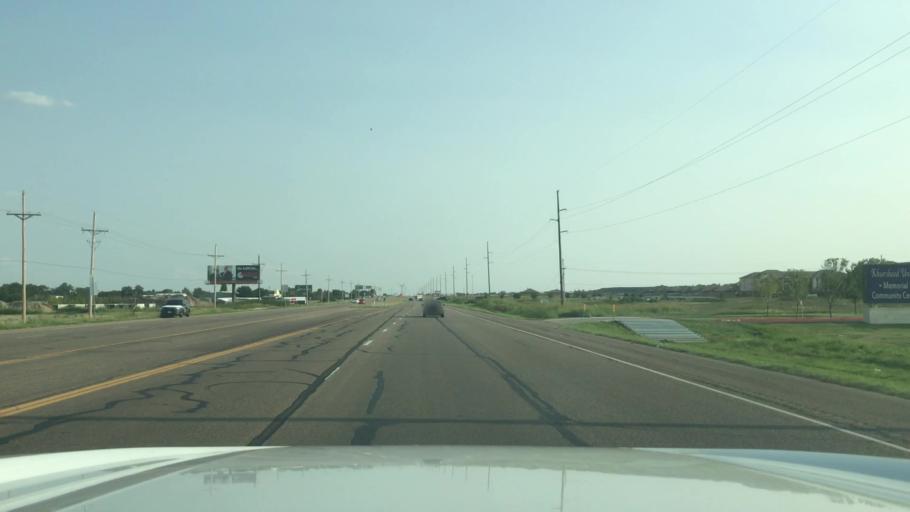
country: US
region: Texas
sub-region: Potter County
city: Amarillo
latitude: 35.1340
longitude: -101.9382
